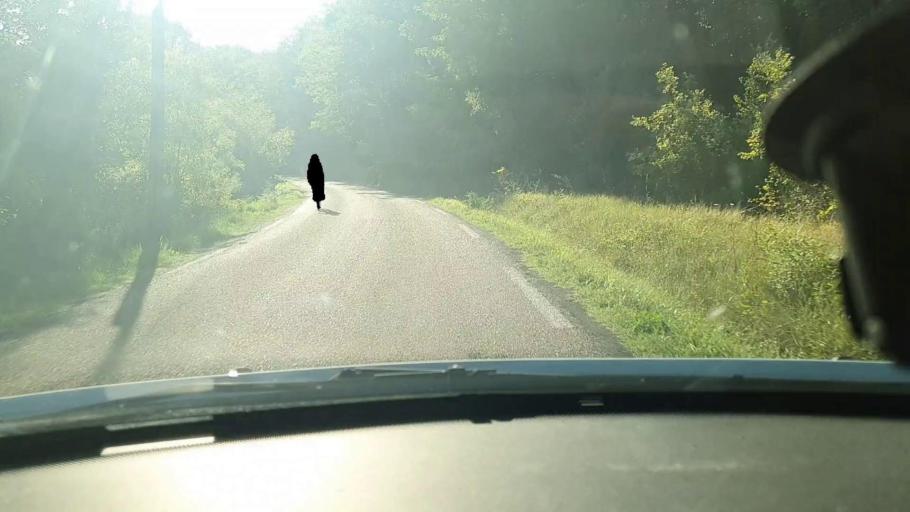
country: FR
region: Languedoc-Roussillon
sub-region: Departement du Gard
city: Goudargues
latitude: 44.1975
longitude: 4.4751
